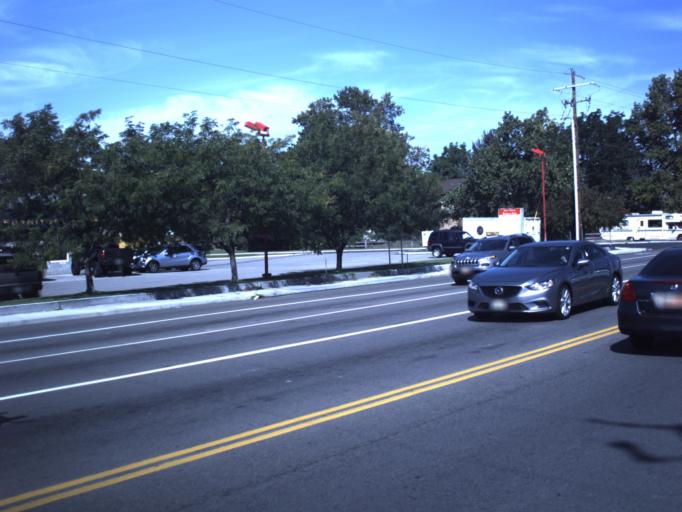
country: US
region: Utah
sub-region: Utah County
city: American Fork
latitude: 40.3704
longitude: -111.7691
